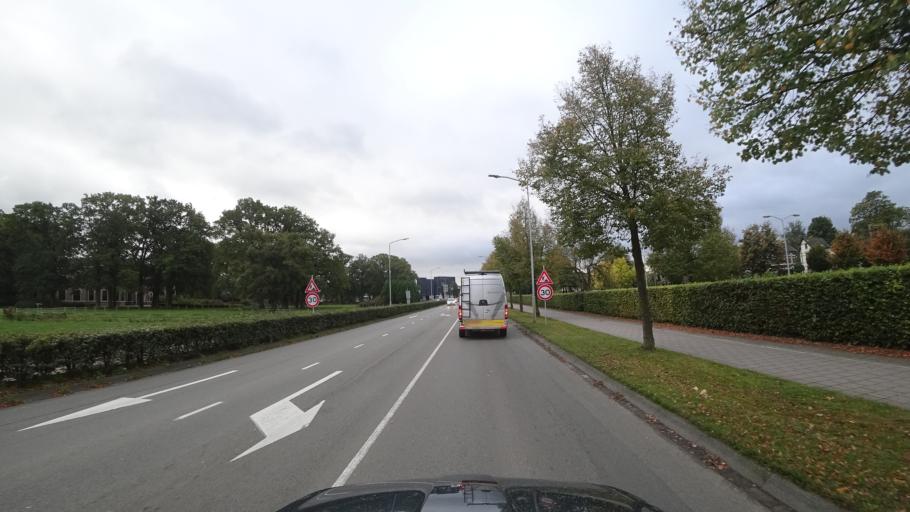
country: NL
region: Gelderland
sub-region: Gemeente Barneveld
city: Barneveld
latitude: 52.1435
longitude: 5.5893
